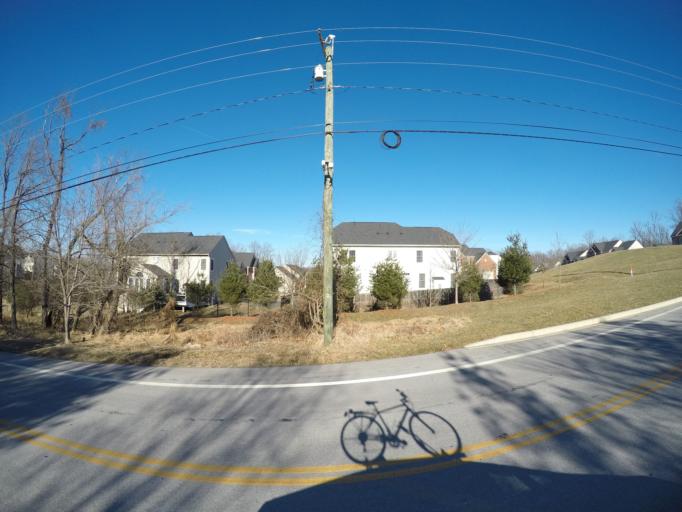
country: US
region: Maryland
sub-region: Howard County
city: Ellicott City
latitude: 39.2556
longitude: -76.7890
